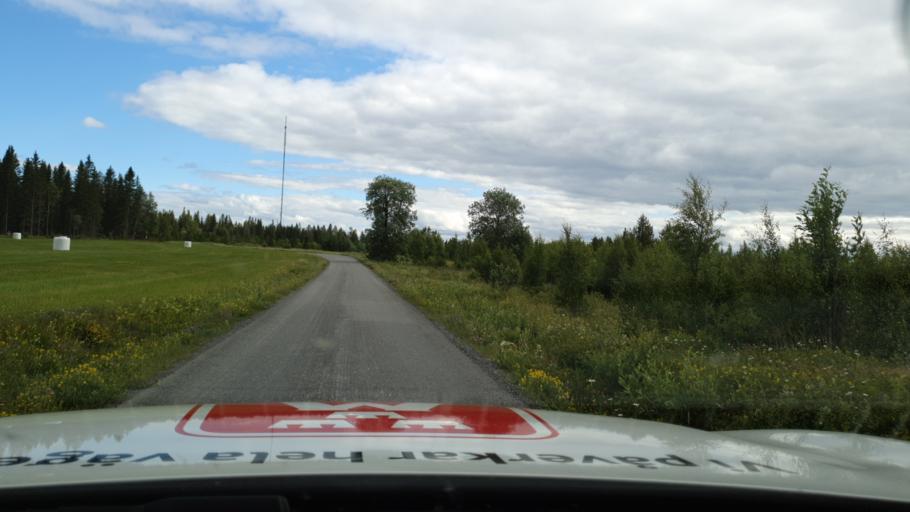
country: SE
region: Jaemtland
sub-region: OEstersunds Kommun
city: Ostersund
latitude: 63.1267
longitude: 14.5823
